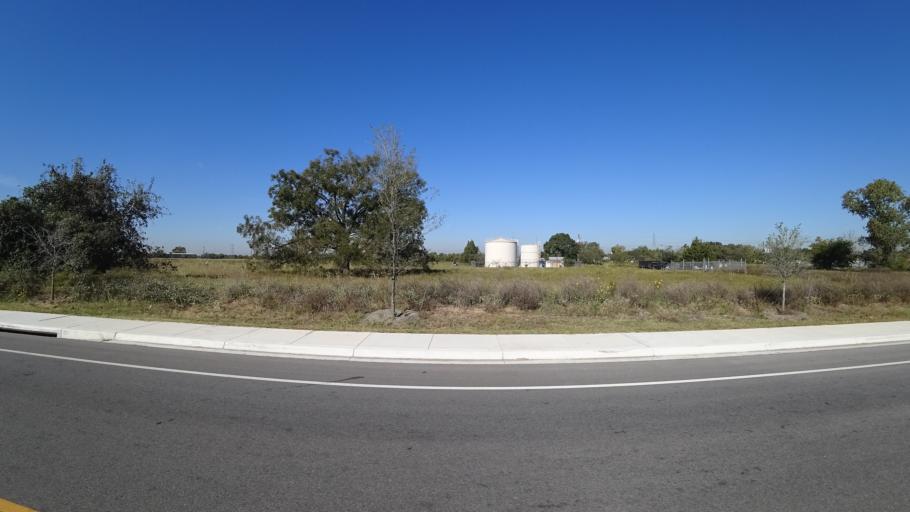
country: US
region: Texas
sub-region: Travis County
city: Hornsby Bend
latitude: 30.2498
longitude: -97.5965
